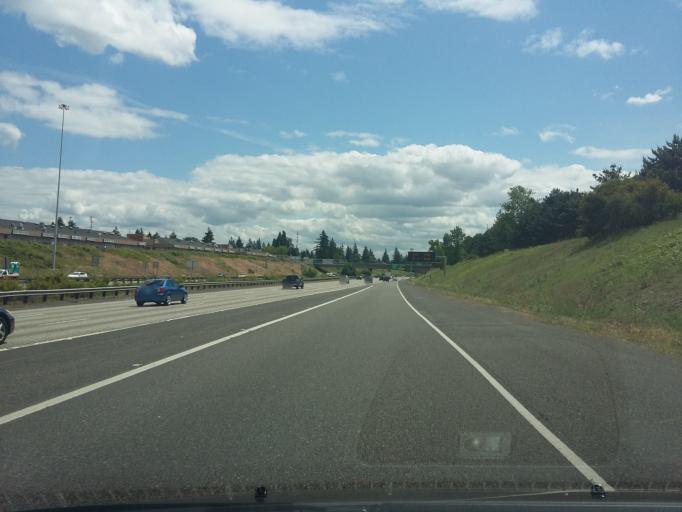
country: US
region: Washington
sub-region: Clark County
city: Orchards
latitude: 45.6176
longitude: -122.5578
